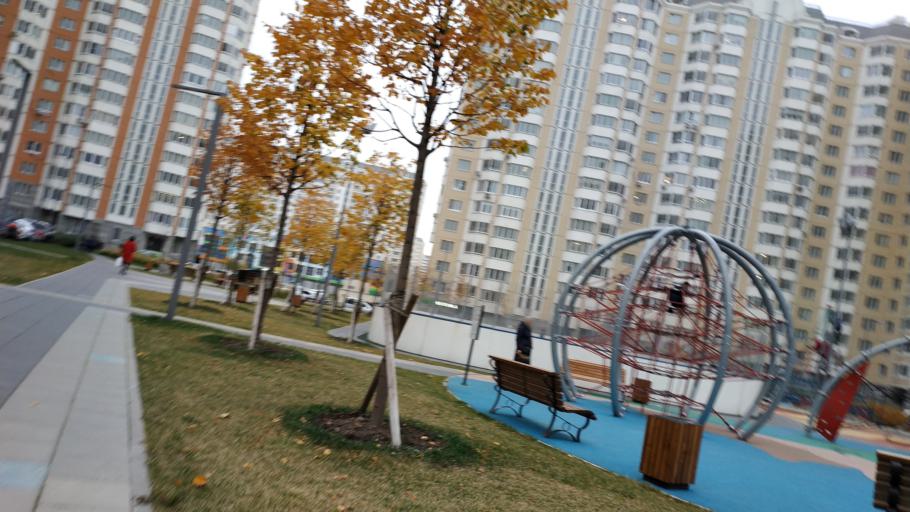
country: RU
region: Moscow
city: Novo-Peredelkino
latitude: 55.6361
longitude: 37.3206
